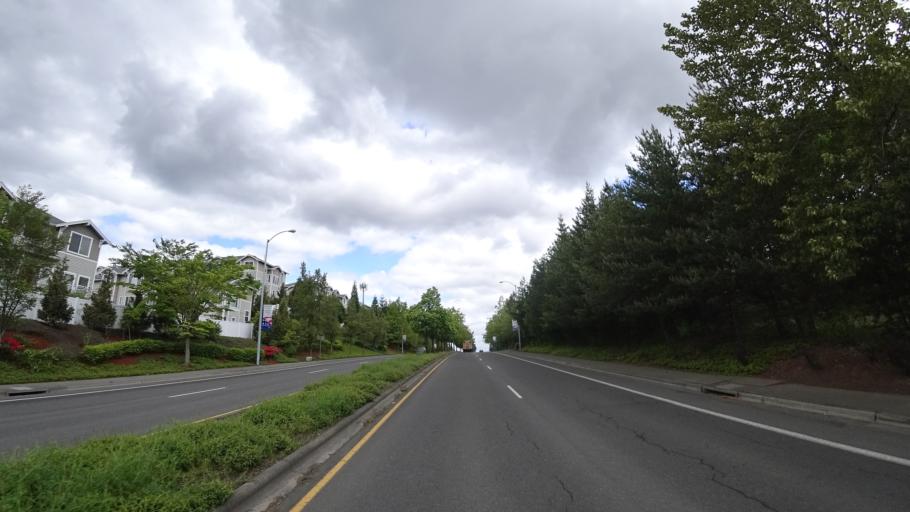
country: US
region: Oregon
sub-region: Washington County
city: Beaverton
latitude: 45.4567
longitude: -122.8262
